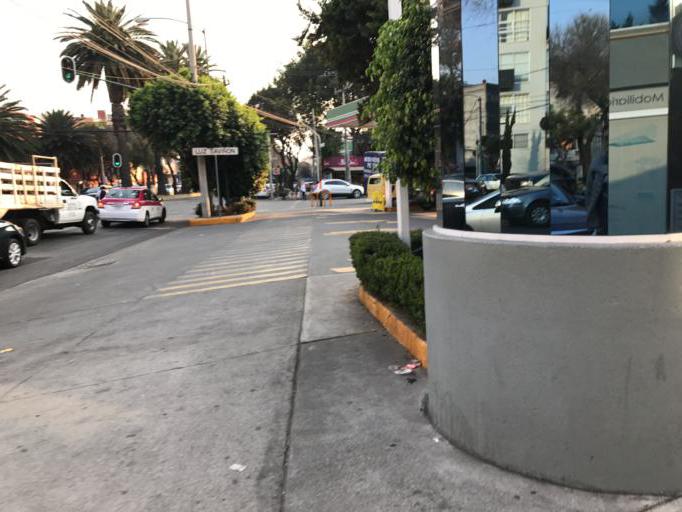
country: MX
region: Mexico City
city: Benito Juarez
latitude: 19.3906
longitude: -99.1524
